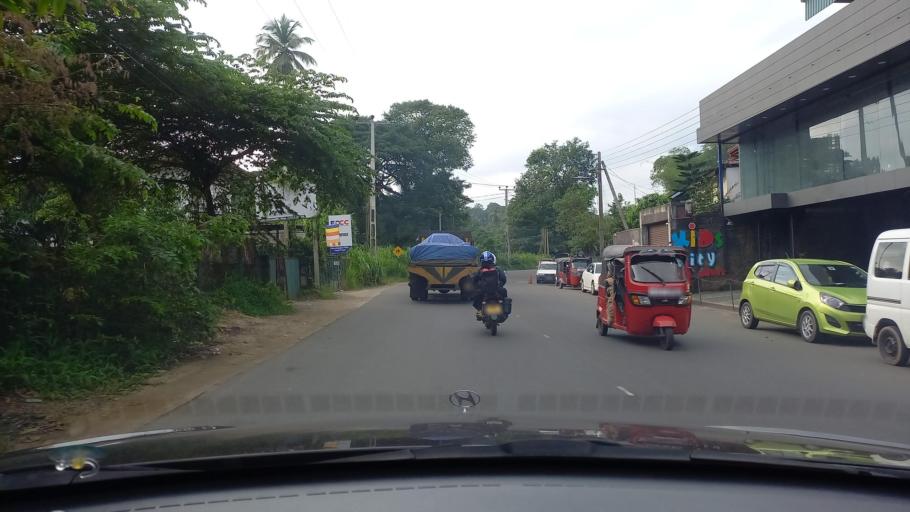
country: LK
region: Central
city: Kadugannawa
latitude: 7.2490
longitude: 80.4636
